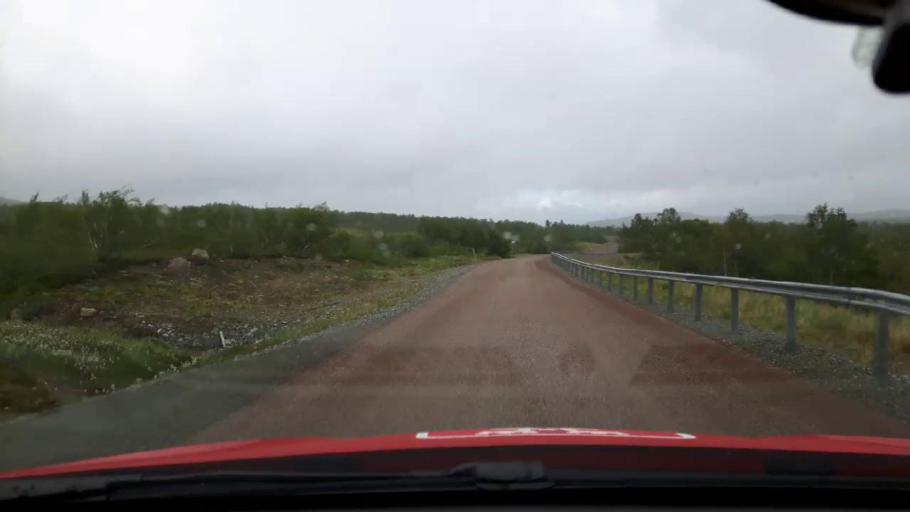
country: NO
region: Nord-Trondelag
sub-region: Meraker
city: Meraker
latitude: 63.2008
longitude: 12.3914
